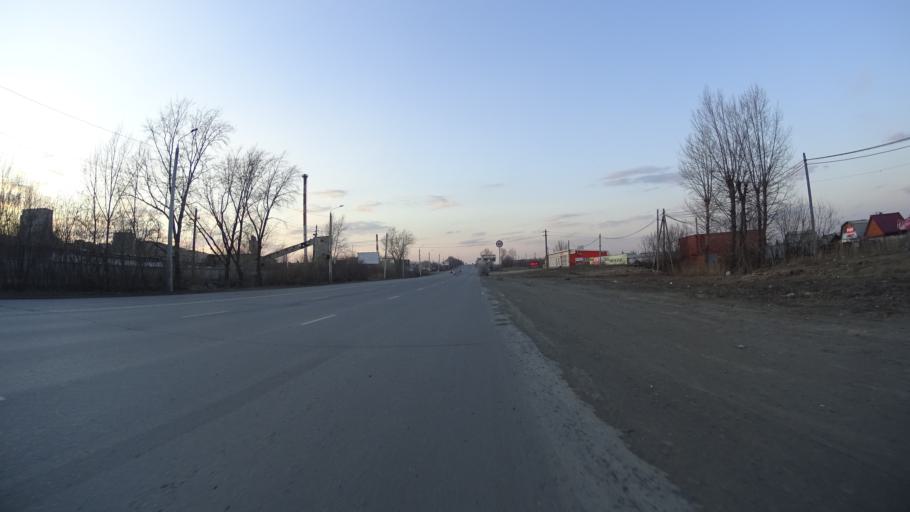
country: RU
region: Chelyabinsk
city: Novosineglazovskiy
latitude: 55.0957
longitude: 61.3881
